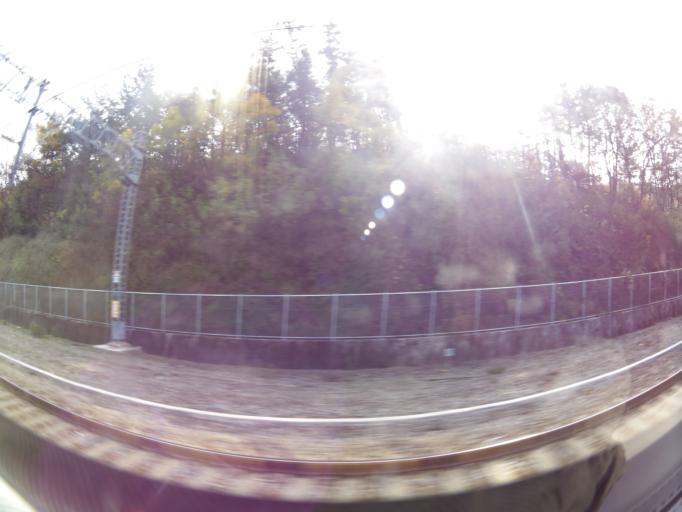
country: KR
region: Daejeon
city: Daejeon
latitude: 36.3367
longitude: 127.4911
